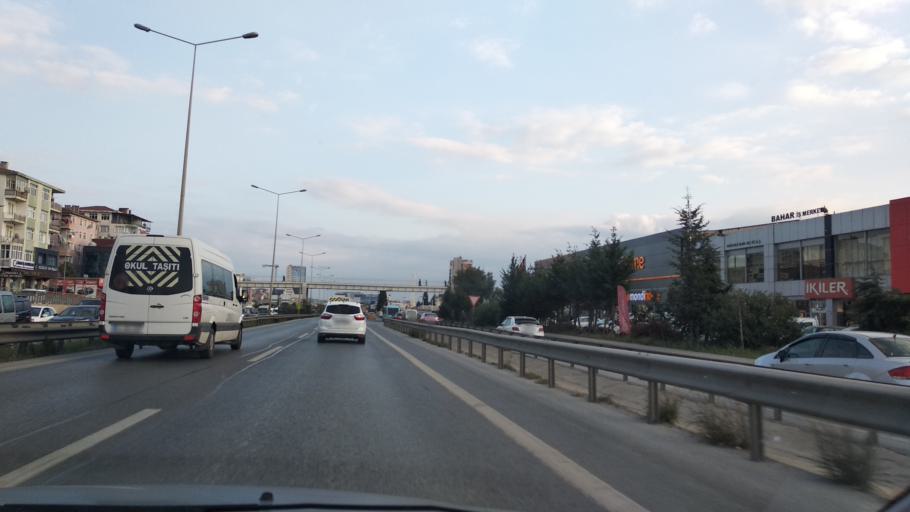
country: TR
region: Istanbul
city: Icmeler
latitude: 40.8538
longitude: 29.2931
